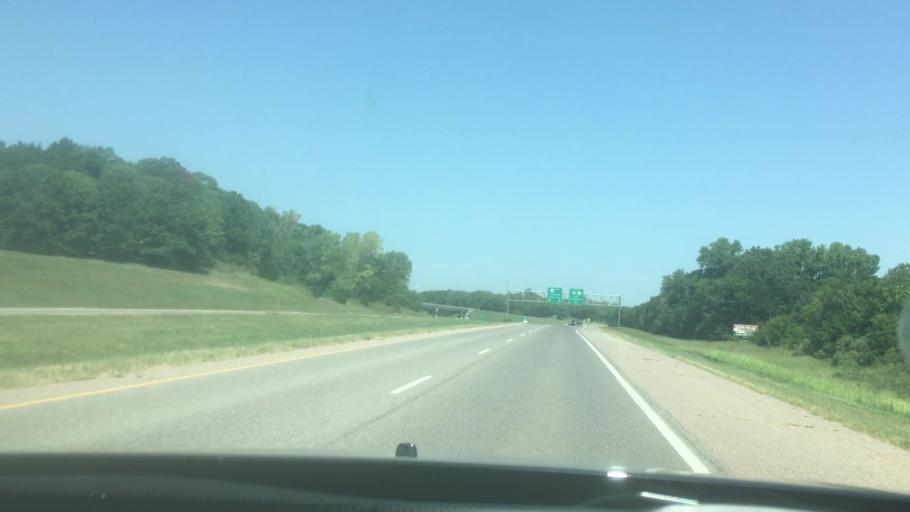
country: US
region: Oklahoma
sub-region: Pontotoc County
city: Ada
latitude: 34.7464
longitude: -96.6522
